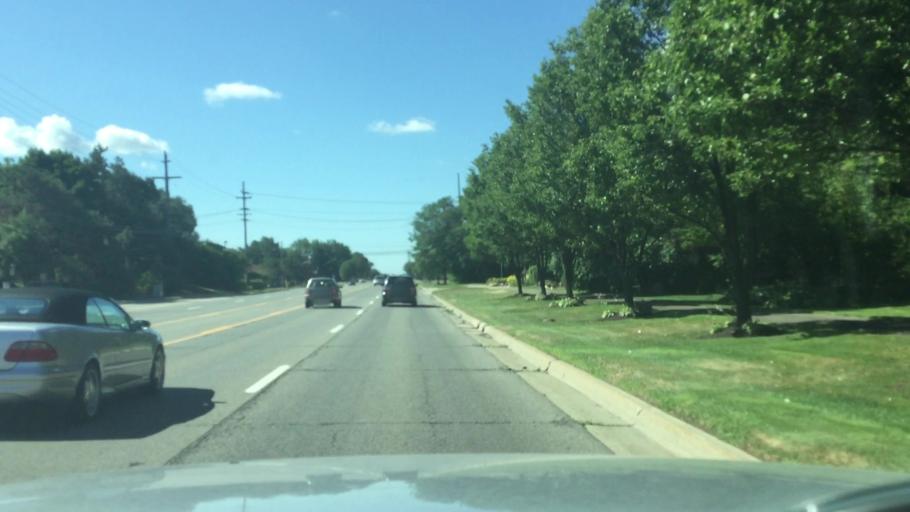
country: US
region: Michigan
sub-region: Oakland County
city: Farmington Hills
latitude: 42.5223
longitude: -83.3599
